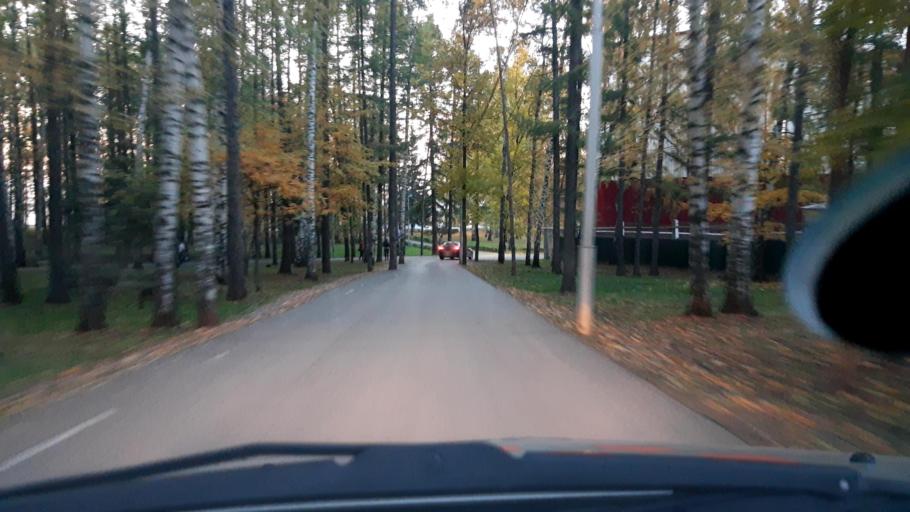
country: RU
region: Bashkortostan
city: Ufa
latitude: 54.8249
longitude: 56.0569
